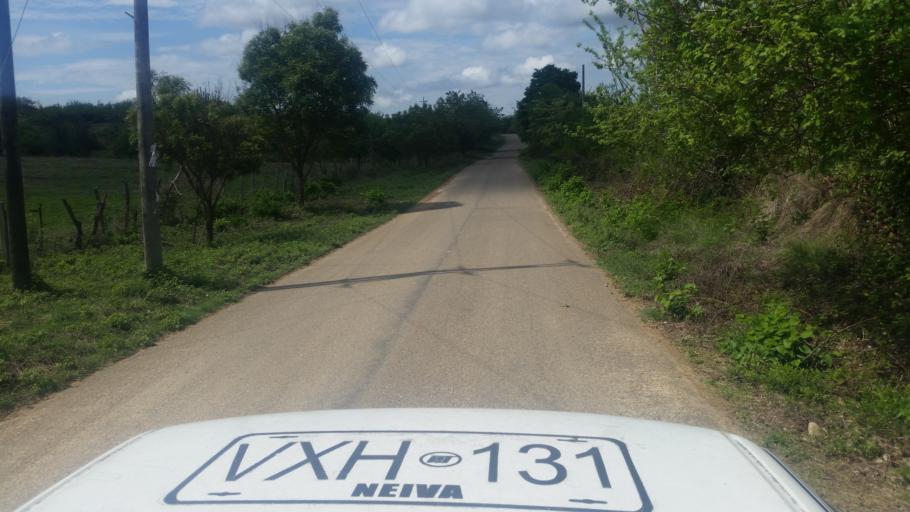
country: CO
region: Huila
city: Villavieja
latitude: 3.1971
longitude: -75.2125
